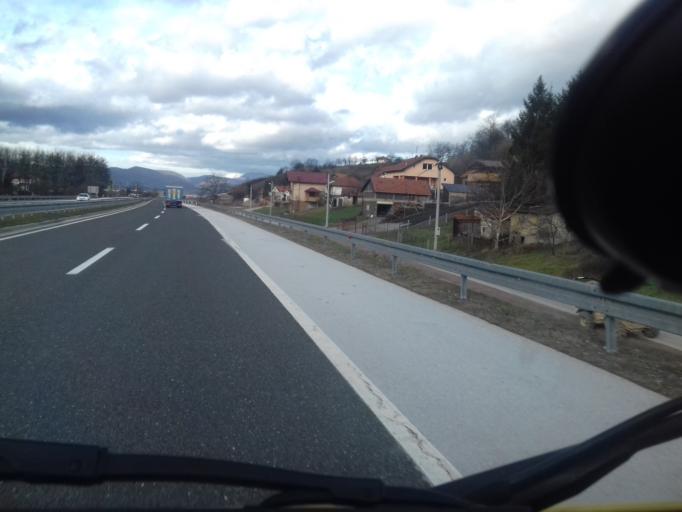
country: BA
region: Federation of Bosnia and Herzegovina
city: Visoko
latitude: 43.9954
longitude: 18.1900
